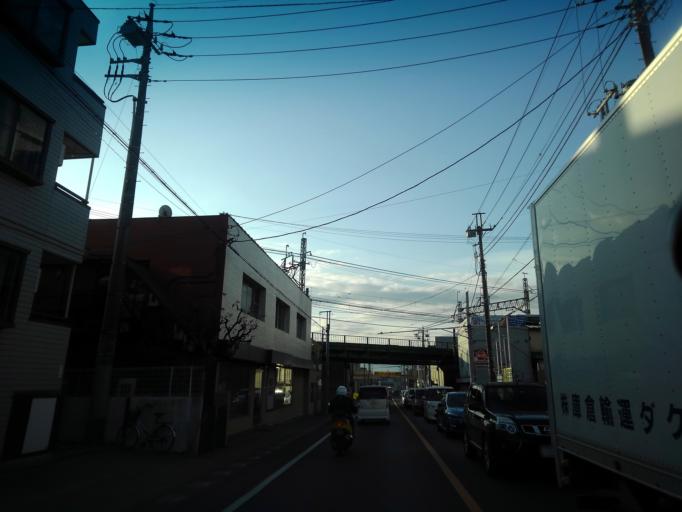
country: JP
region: Saitama
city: Tokorozawa
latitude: 35.7819
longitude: 139.4719
